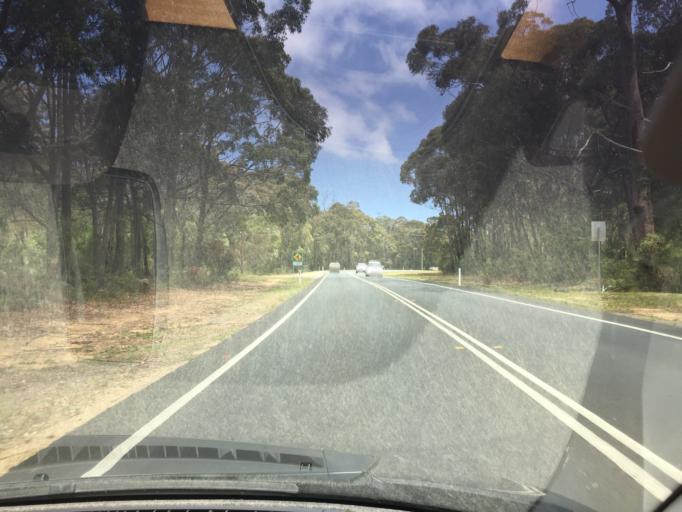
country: AU
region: New South Wales
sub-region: Bega Valley
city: Merimbula
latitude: -36.8642
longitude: 149.9077
